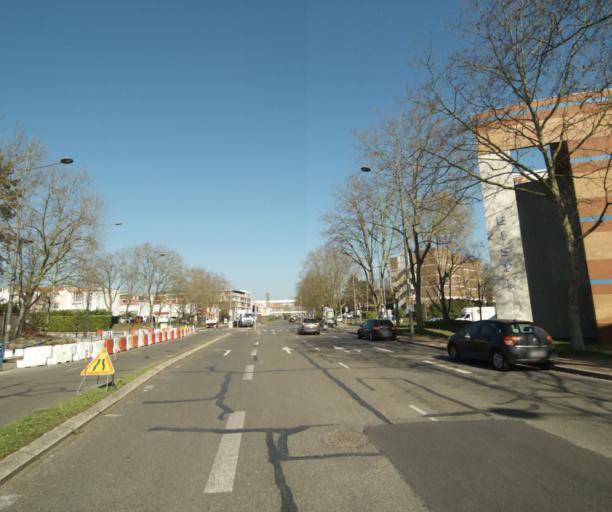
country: FR
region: Ile-de-France
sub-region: Departement du Val-d'Oise
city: Cergy
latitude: 49.0353
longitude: 2.0691
